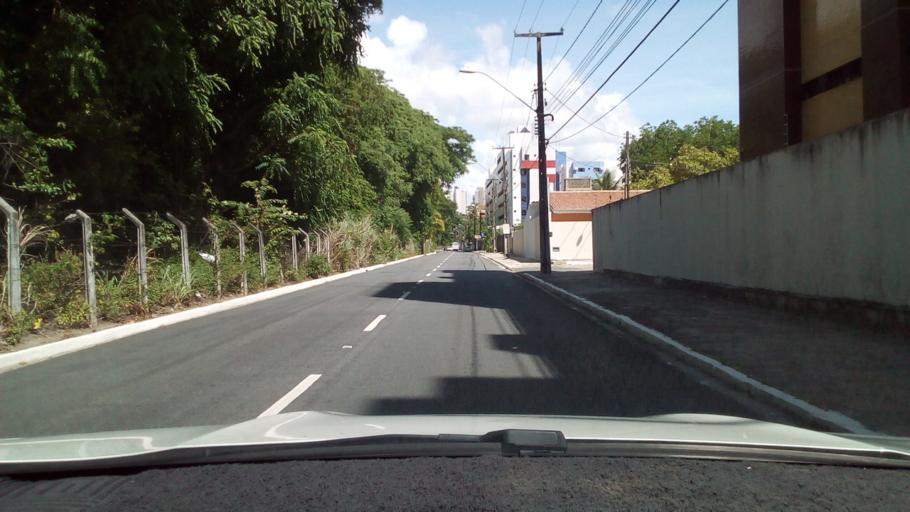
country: BR
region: Paraiba
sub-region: Joao Pessoa
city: Joao Pessoa
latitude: -7.1417
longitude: -34.8165
